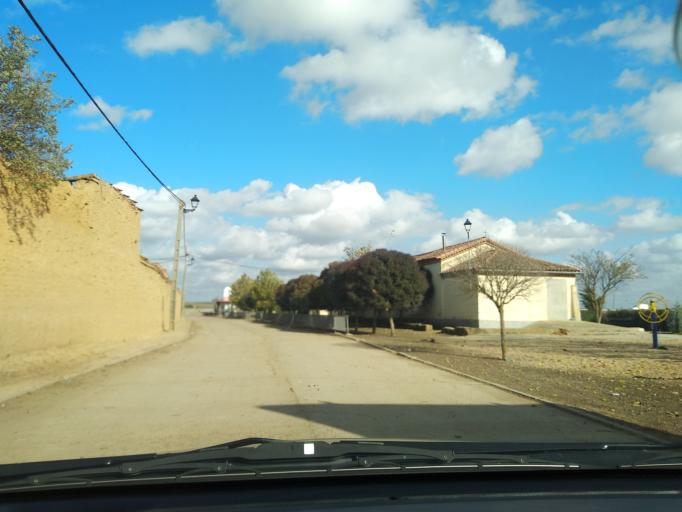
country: ES
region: Castille and Leon
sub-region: Provincia de Valladolid
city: Berrueces
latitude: 41.9456
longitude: -5.0955
